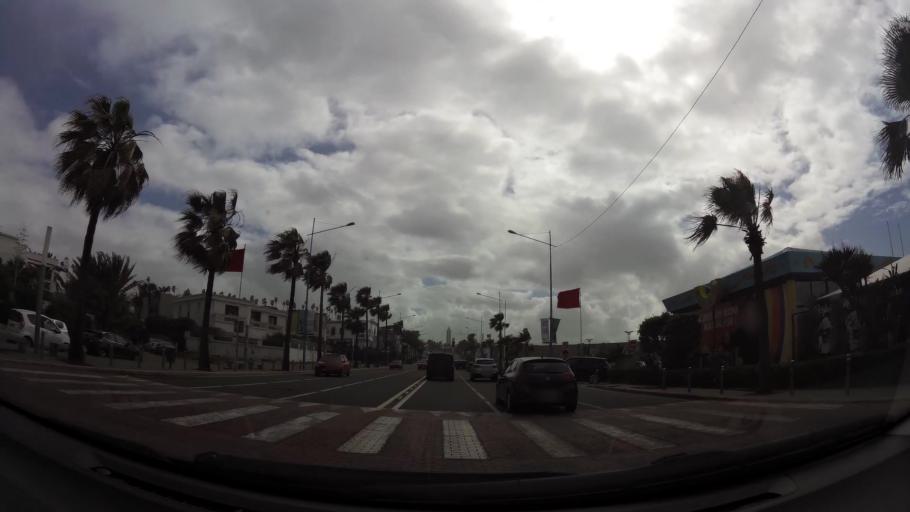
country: MA
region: Grand Casablanca
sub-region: Casablanca
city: Casablanca
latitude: 33.6010
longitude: -7.6615
